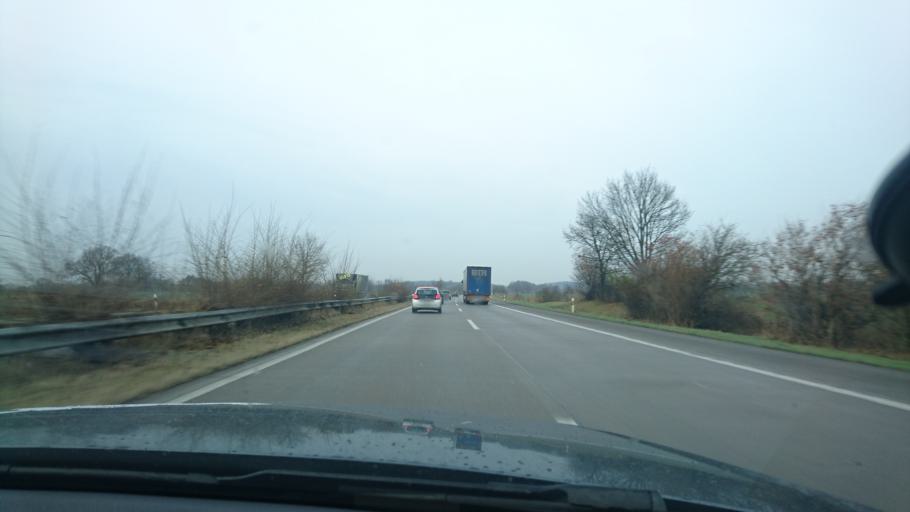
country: DE
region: Schleswig-Holstein
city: Ratekau
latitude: 53.9692
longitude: 10.7346
